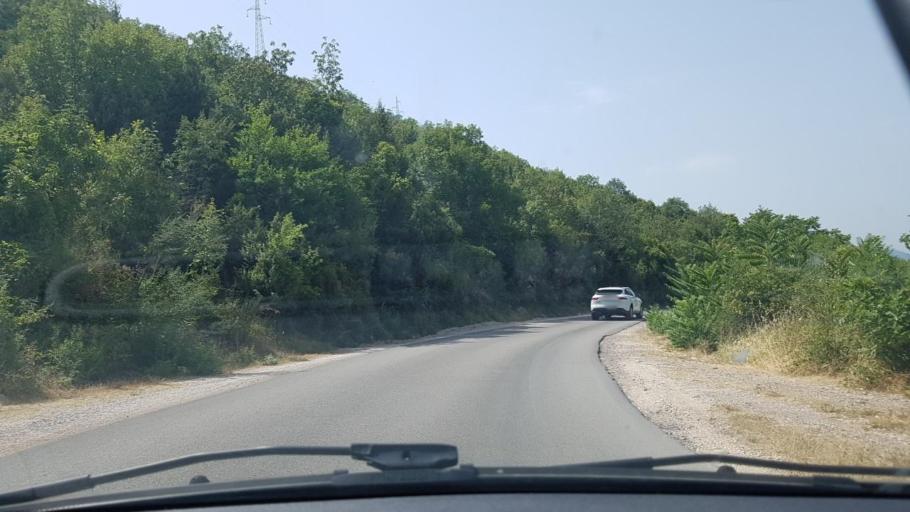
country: BA
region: Federation of Bosnia and Herzegovina
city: Tasovcici
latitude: 43.0308
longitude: 17.7402
